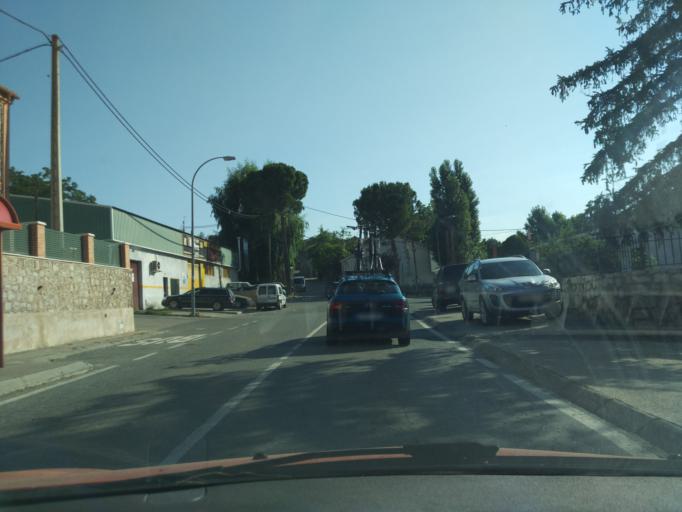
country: ES
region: Madrid
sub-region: Provincia de Madrid
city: Ambite
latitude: 40.3265
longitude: -3.1837
